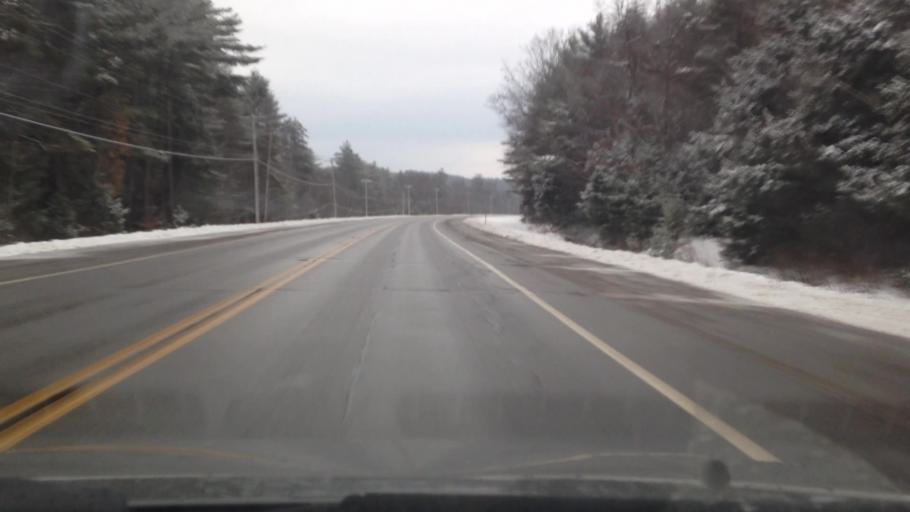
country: US
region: New Hampshire
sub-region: Cheshire County
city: Keene
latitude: 42.9827
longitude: -72.2572
